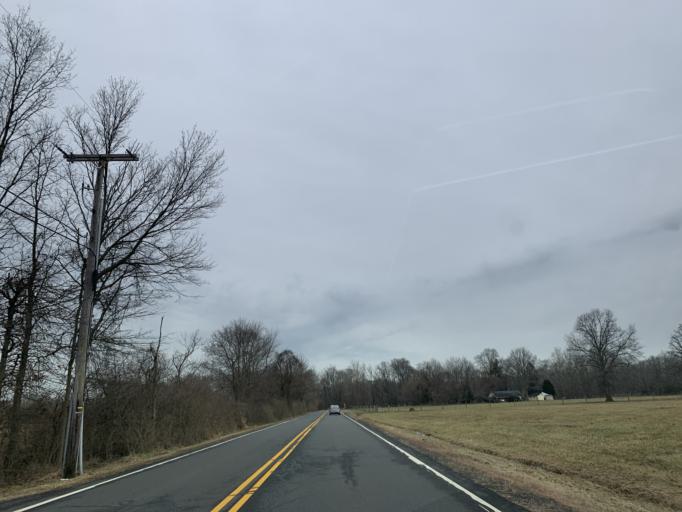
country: US
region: New Jersey
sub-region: Somerset County
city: Bridgewater
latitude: 40.6359
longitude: -74.6767
